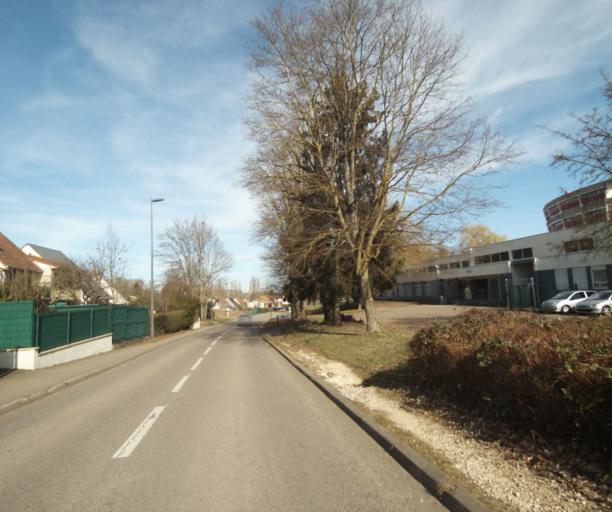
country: FR
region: Lorraine
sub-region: Departement de Meurthe-et-Moselle
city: Villers-les-Nancy
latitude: 48.6640
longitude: 6.1556
